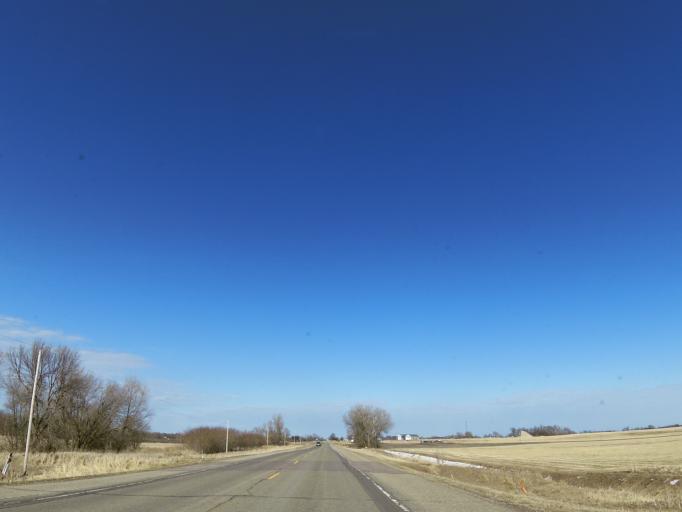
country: US
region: Minnesota
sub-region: Le Sueur County
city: Montgomery
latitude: 44.4172
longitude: -93.5912
